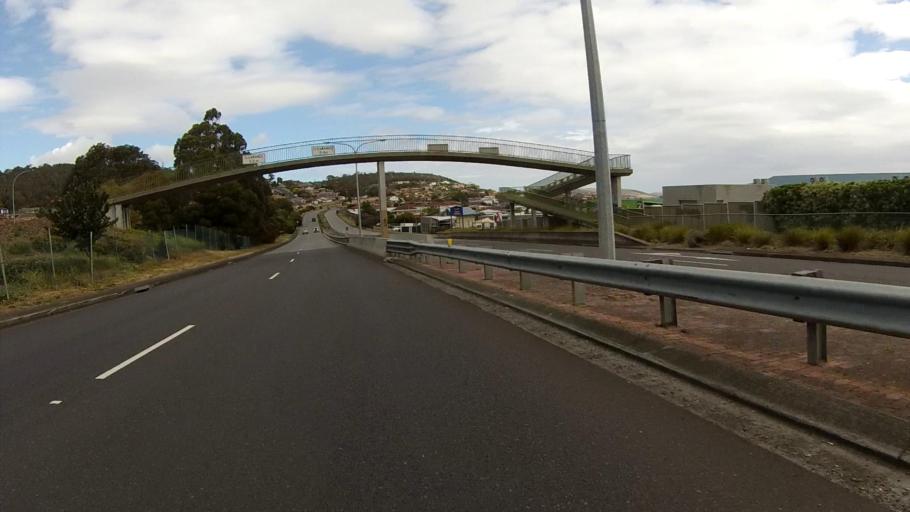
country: AU
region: Tasmania
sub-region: Clarence
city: Howrah
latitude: -42.8784
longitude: 147.4070
